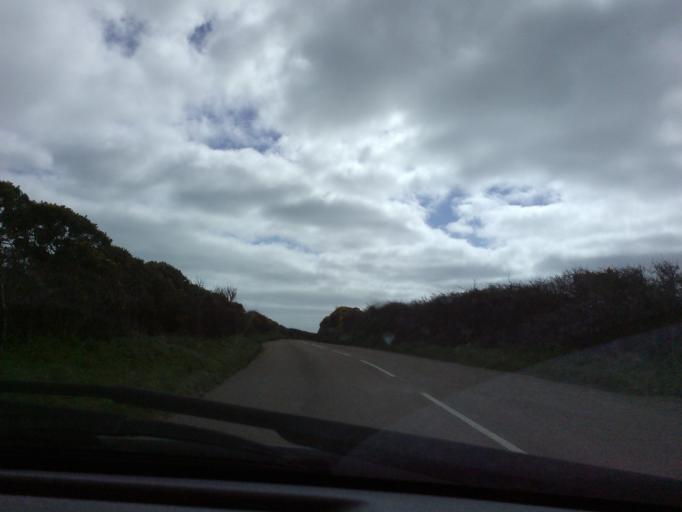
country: GB
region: England
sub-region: Cornwall
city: St. Buryan
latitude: 50.0579
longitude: -5.6372
